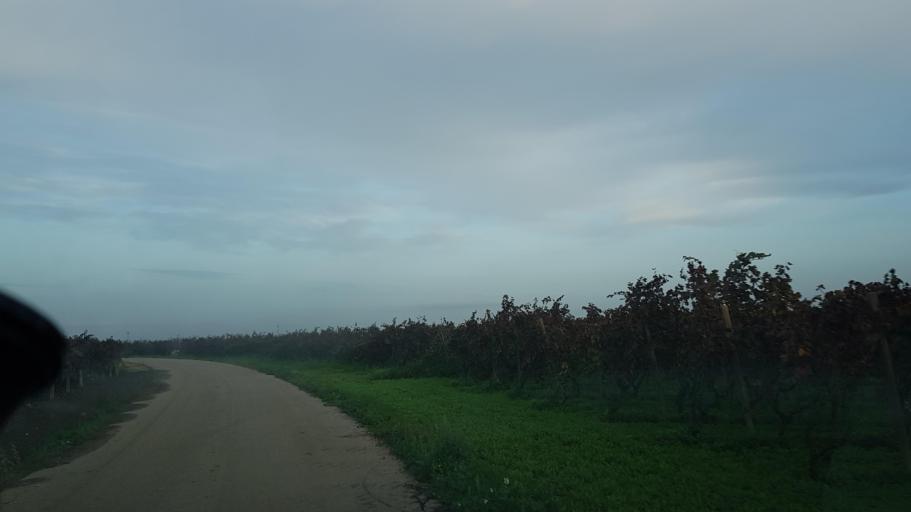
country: IT
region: Apulia
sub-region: Provincia di Brindisi
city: San Pancrazio Salentino
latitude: 40.4212
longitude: 17.8635
